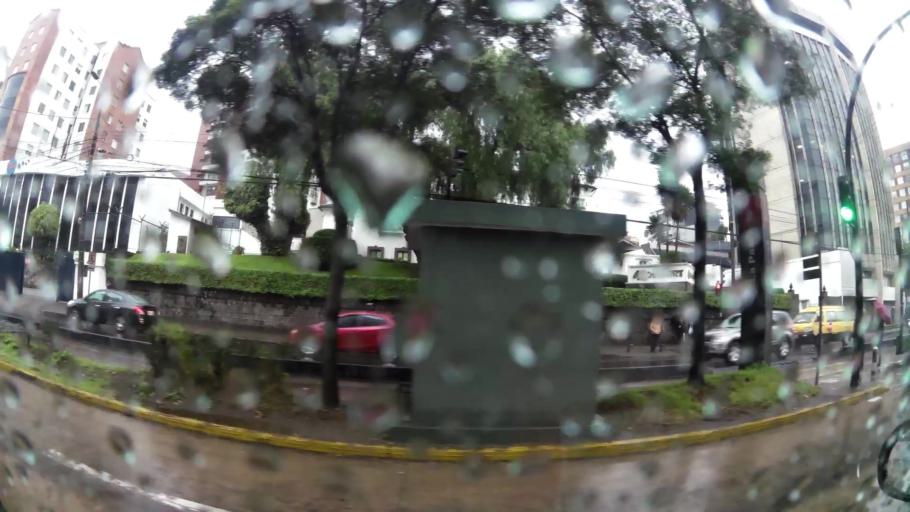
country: EC
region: Pichincha
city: Quito
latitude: -0.1958
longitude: -78.4829
